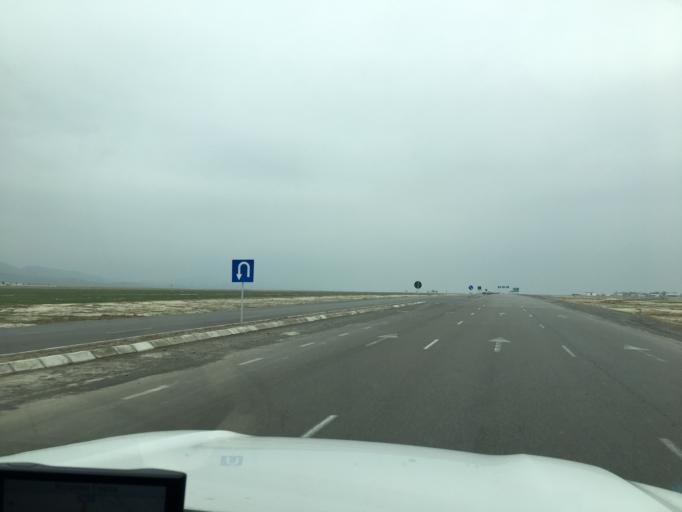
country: IR
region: Razavi Khorasan
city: Dargaz
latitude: 37.7154
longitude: 59.0189
